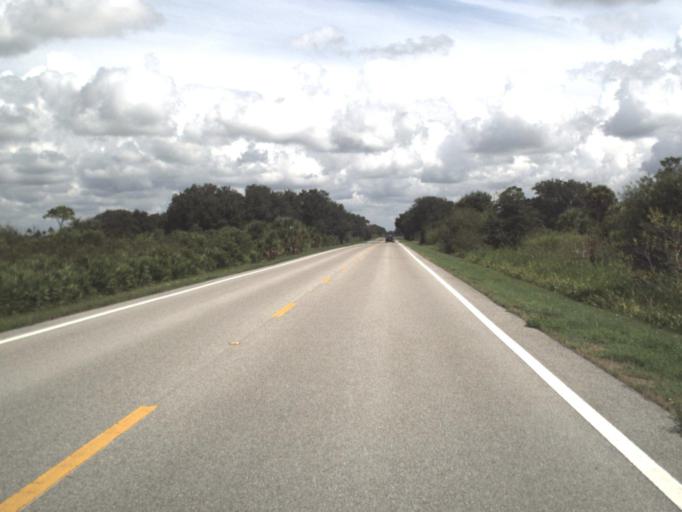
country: US
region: Florida
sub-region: Sarasota County
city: Warm Mineral Springs
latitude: 27.2196
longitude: -82.2839
